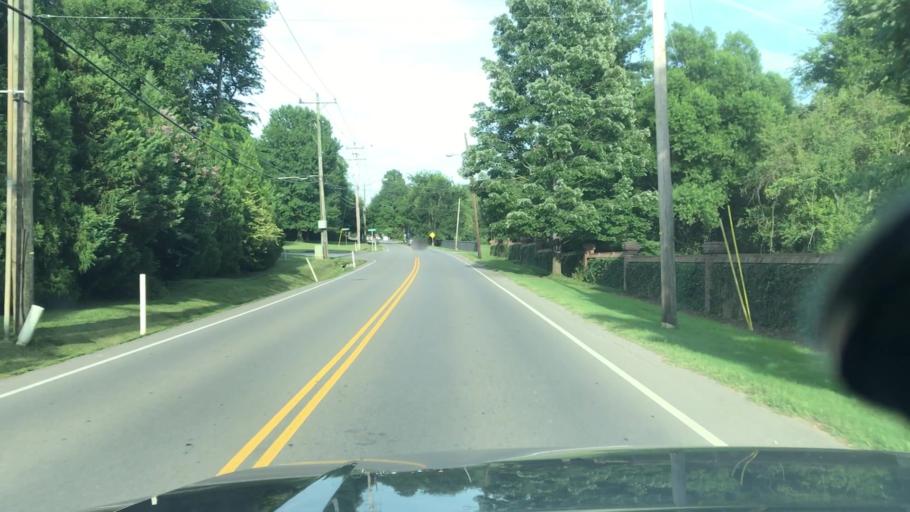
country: US
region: Tennessee
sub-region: Davidson County
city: Belle Meade
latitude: 36.0916
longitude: -86.8334
